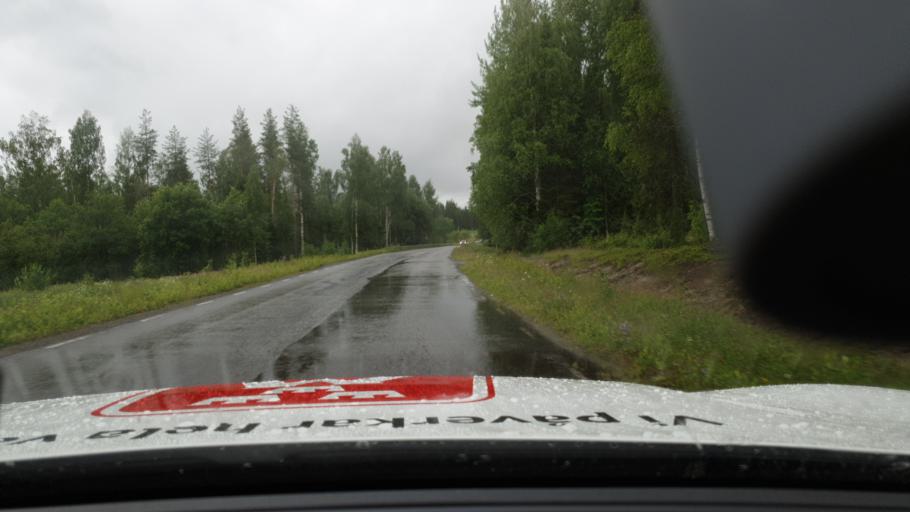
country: SE
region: Norrbotten
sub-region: Bodens Kommun
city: Boden
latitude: 65.8758
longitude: 21.3799
